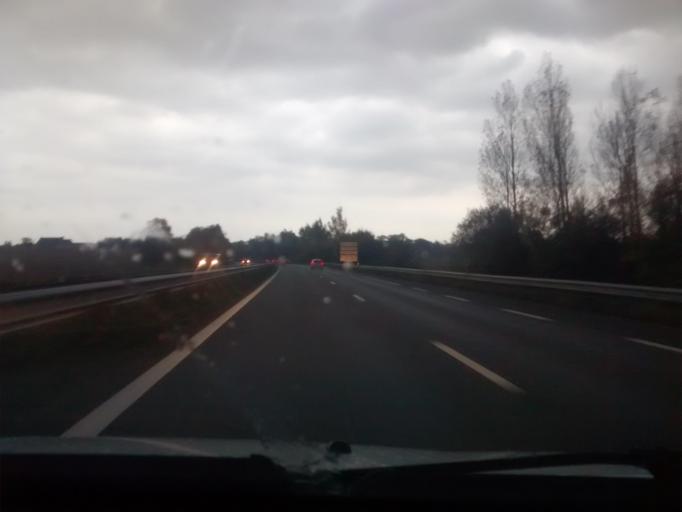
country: FR
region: Brittany
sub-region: Departement d'Ille-et-Vilaine
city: Saint-Domineuc
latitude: 48.3724
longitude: -1.8884
